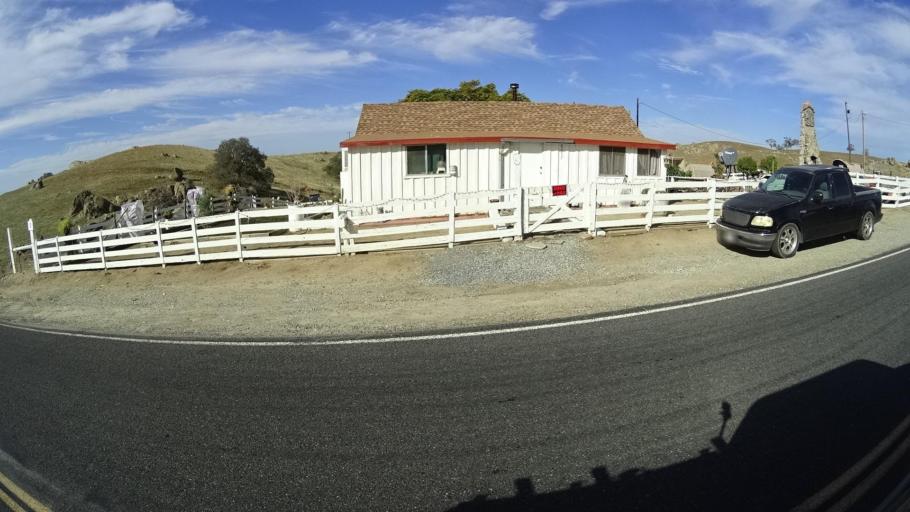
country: US
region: California
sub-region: Kern County
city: Oildale
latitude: 35.6137
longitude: -118.8594
